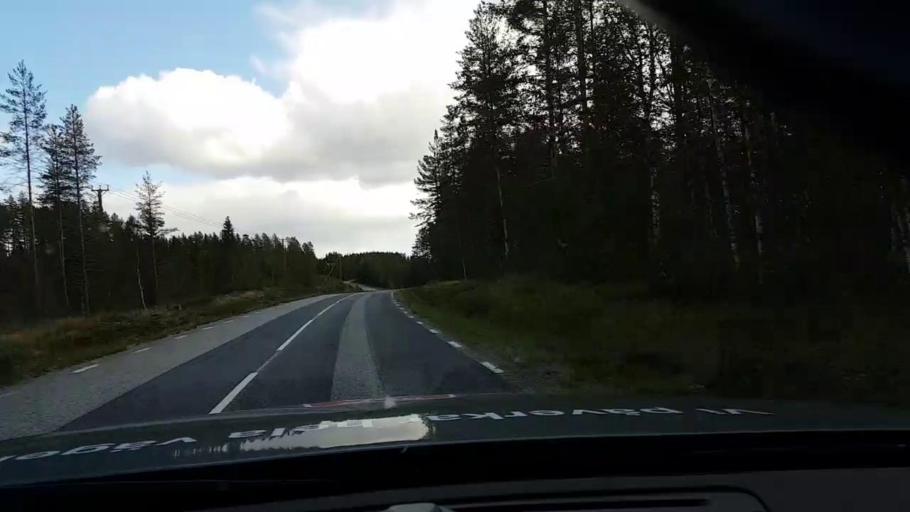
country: SE
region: Vaesterbotten
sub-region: Asele Kommun
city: Asele
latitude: 63.8100
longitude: 17.5297
